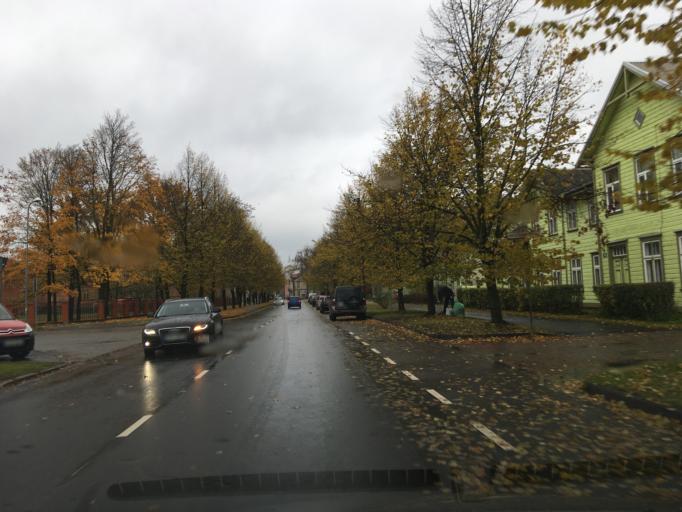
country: EE
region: Paernumaa
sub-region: Paernu linn
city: Parnu
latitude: 58.3819
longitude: 24.5065
